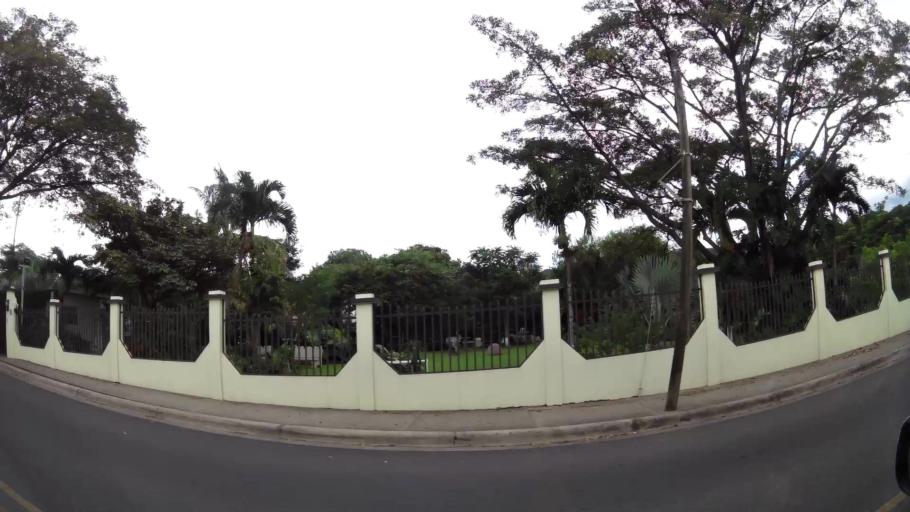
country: CR
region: Heredia
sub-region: Canton de Belen
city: San Antonio
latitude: 9.9584
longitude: -84.1907
